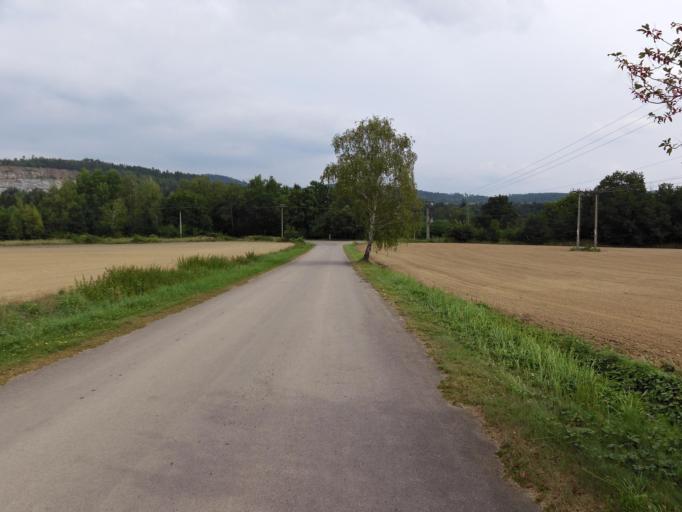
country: CZ
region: Central Bohemia
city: Kamenny Privoz
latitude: 49.8520
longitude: 14.5460
